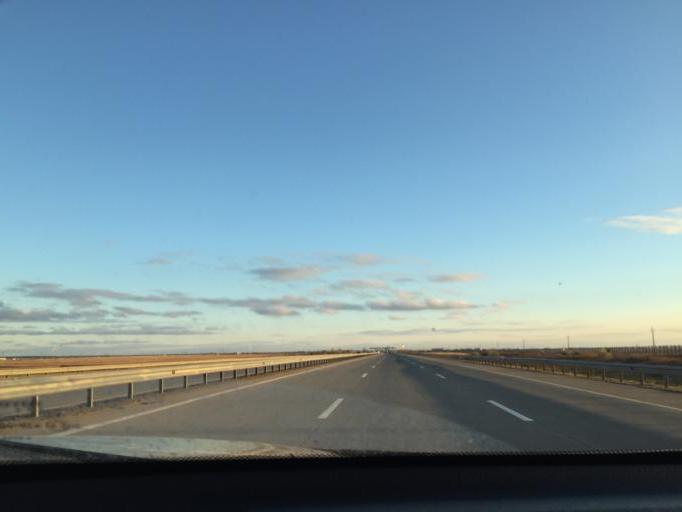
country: KZ
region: Astana Qalasy
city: Astana
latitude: 51.2807
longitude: 71.3633
